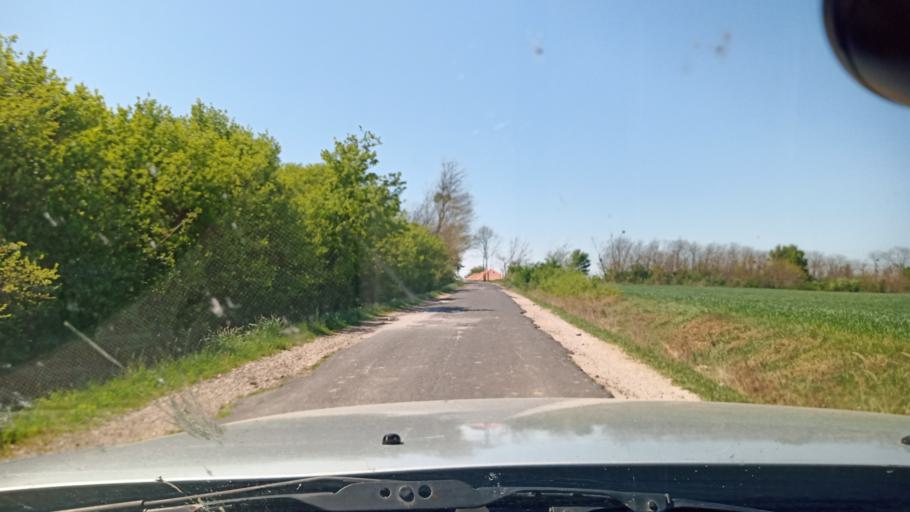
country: HU
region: Zala
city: Heviz
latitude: 46.7667
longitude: 17.1503
